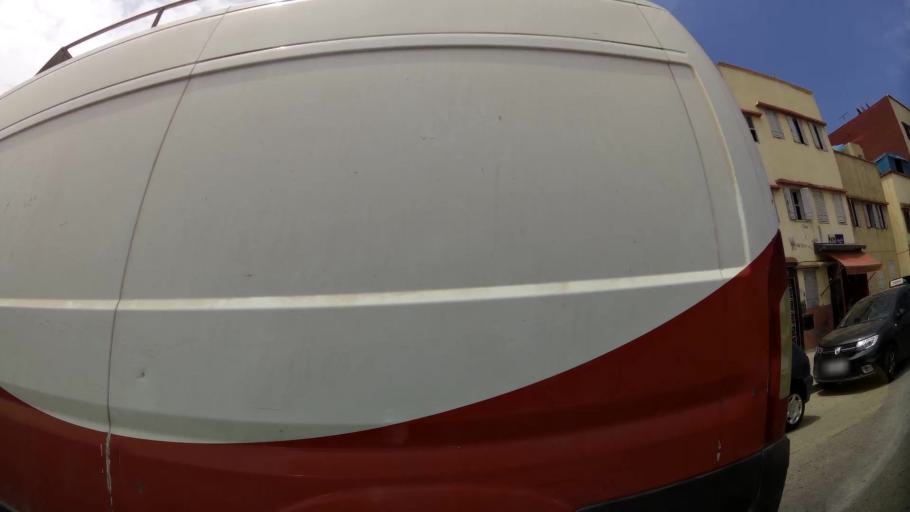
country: MA
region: Rabat-Sale-Zemmour-Zaer
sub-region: Rabat
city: Rabat
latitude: 33.9871
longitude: -6.8857
